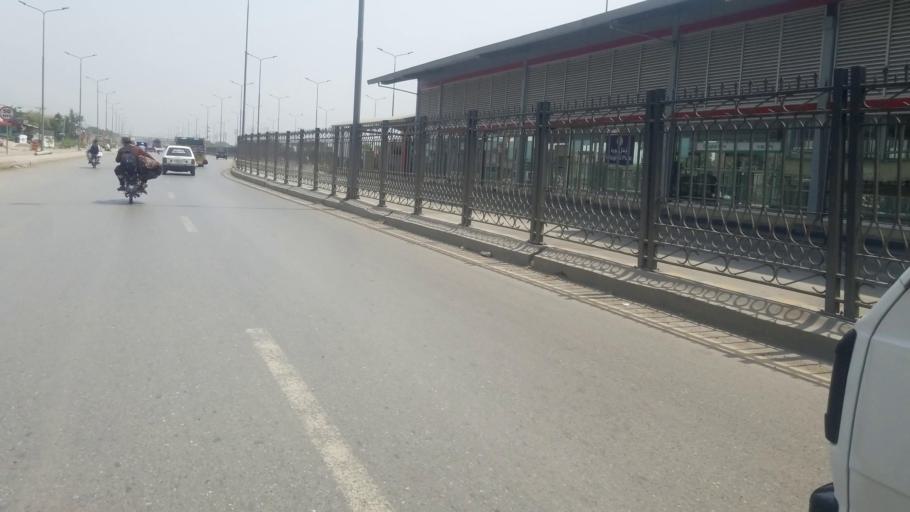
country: PK
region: Khyber Pakhtunkhwa
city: Peshawar
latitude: 34.0177
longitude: 71.6294
